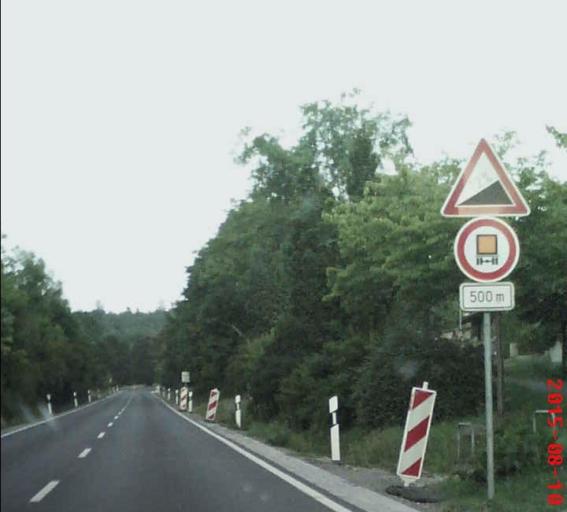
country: DE
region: Thuringia
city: Meiningen
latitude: 50.5688
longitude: 10.4275
